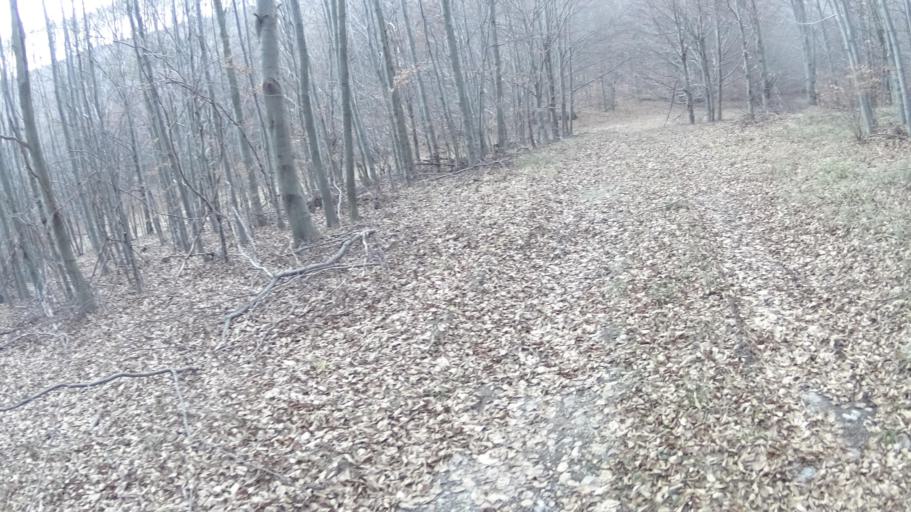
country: HU
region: Heves
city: Szilvasvarad
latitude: 48.0855
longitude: 20.4827
